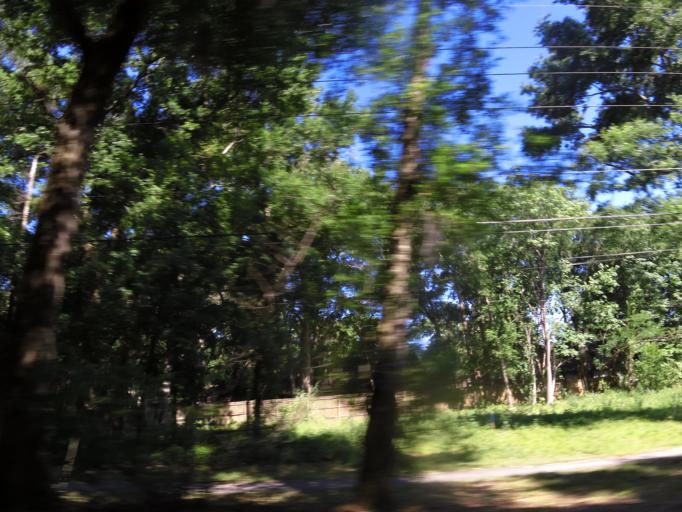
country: US
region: Florida
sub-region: Duval County
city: Atlantic Beach
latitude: 30.3608
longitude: -81.5158
